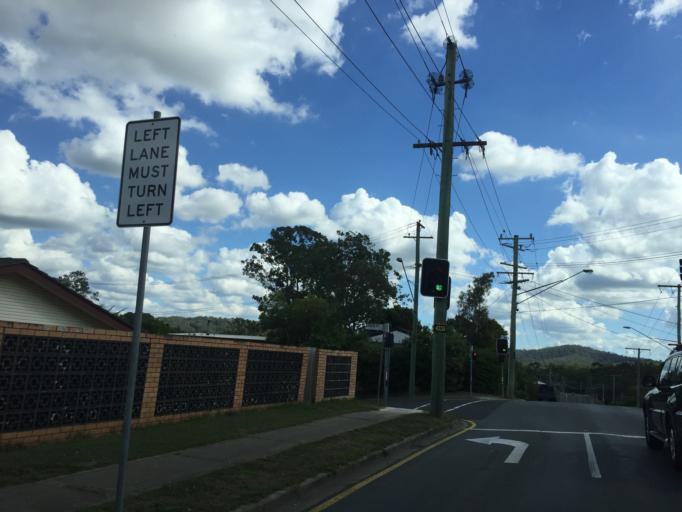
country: AU
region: Queensland
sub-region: Moreton Bay
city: Ferny Hills
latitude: -27.3944
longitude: 152.9385
